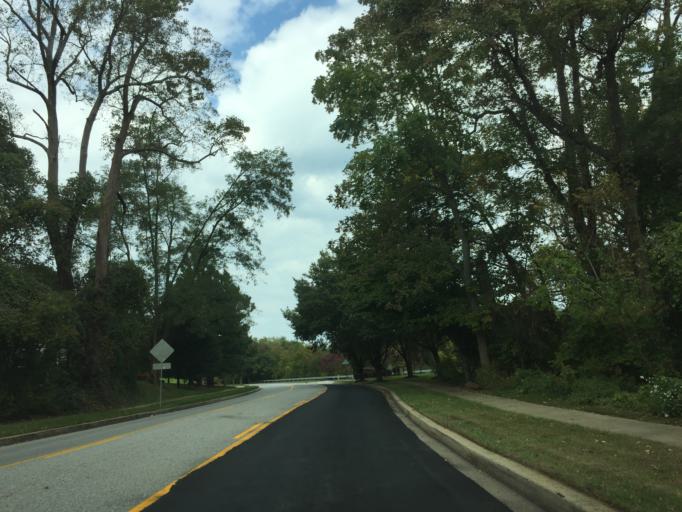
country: US
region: Maryland
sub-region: Harford County
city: Bel Air South
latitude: 39.4953
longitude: -76.3178
